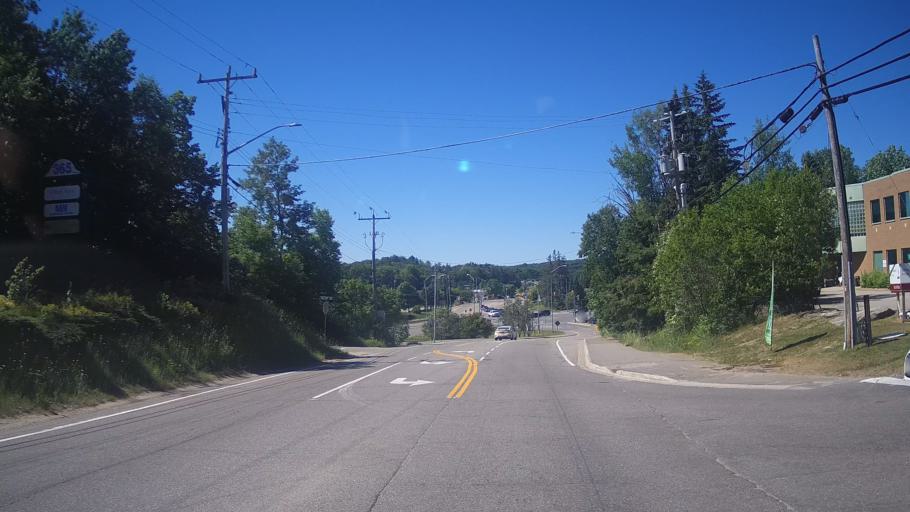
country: CA
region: Ontario
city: Huntsville
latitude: 45.3386
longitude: -79.2025
